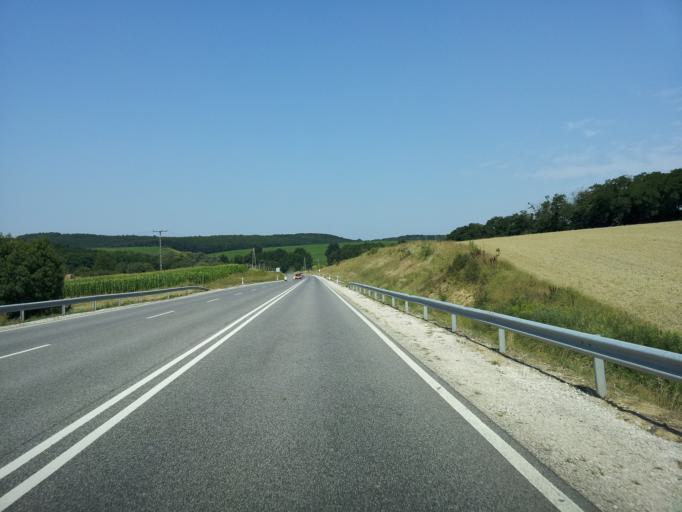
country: HU
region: Zala
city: Zalaszentgrot
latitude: 46.8348
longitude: 17.0393
